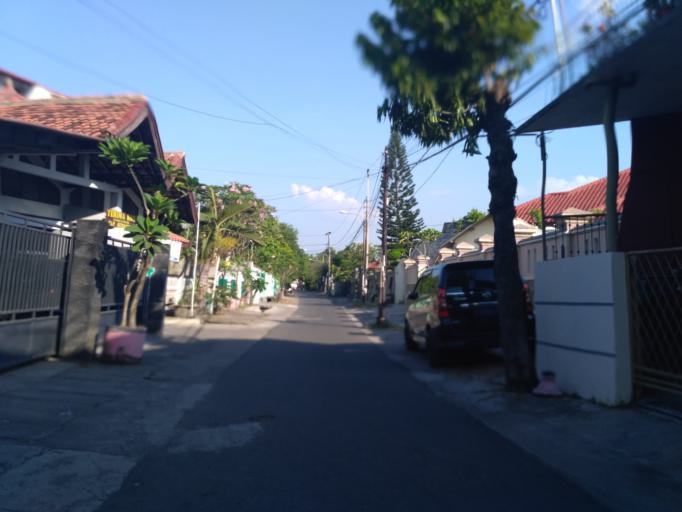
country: ID
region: Central Java
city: Semarang
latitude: -6.9948
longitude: 110.4501
